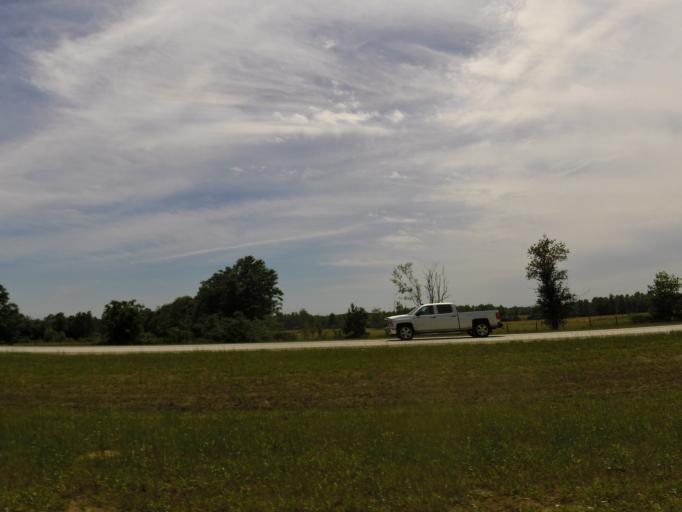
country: US
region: Georgia
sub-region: Candler County
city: Metter
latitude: 32.3595
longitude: -81.9966
